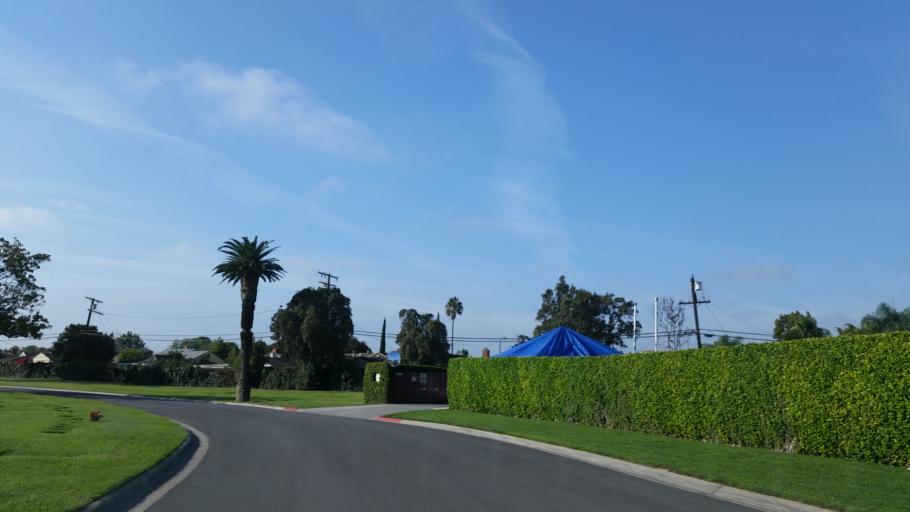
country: US
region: California
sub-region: Los Angeles County
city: Lakewood
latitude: 33.8437
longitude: -118.1708
